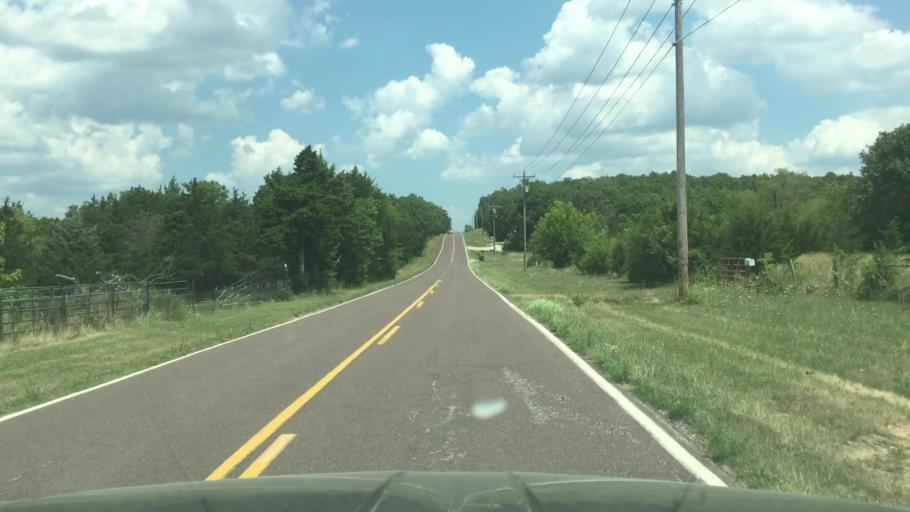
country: US
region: Missouri
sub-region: Miller County
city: Tuscumbia
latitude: 38.1097
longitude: -92.4729
